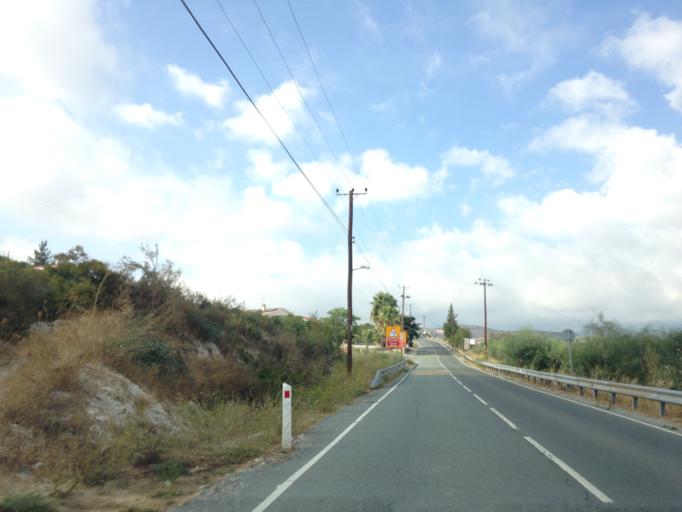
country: CY
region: Limassol
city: Pachna
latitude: 34.8413
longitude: 32.8082
